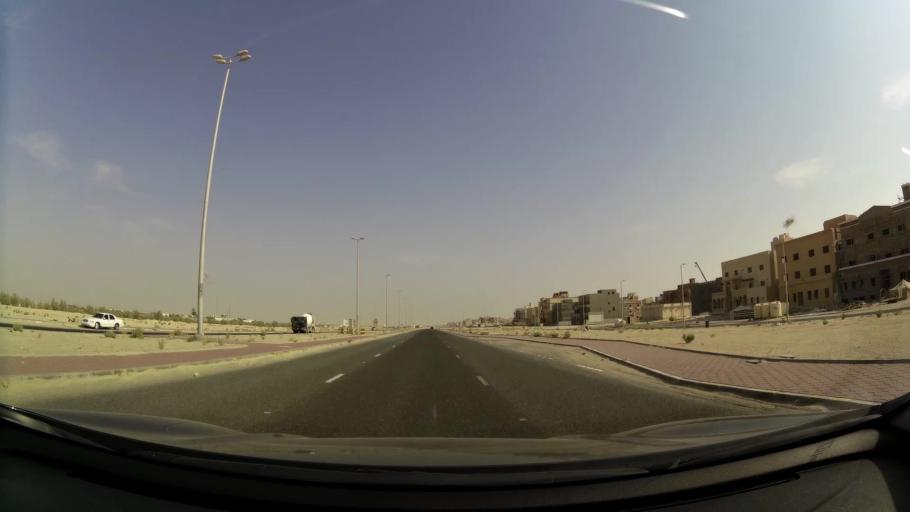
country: KW
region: Al Ahmadi
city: Al Wafrah
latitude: 28.7865
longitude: 48.0353
